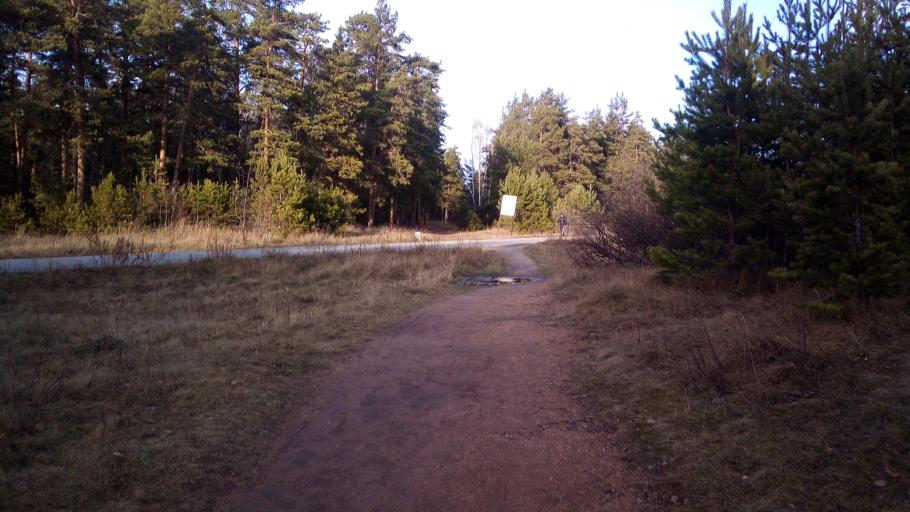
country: RU
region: Chelyabinsk
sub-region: Gorod Chelyabinsk
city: Chelyabinsk
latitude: 55.1552
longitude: 61.3511
